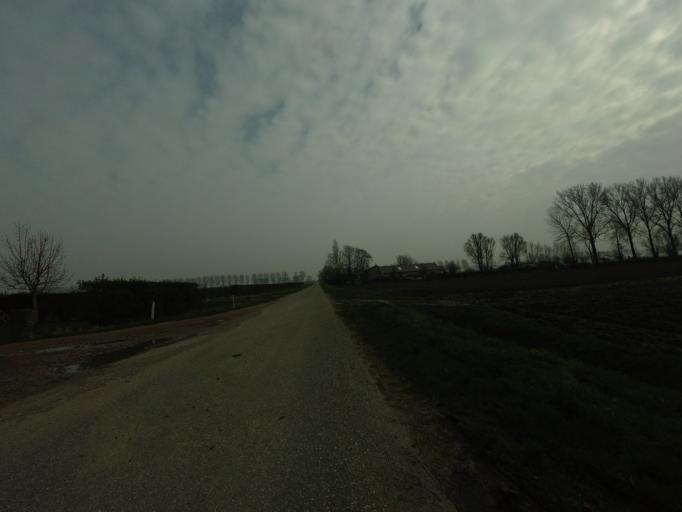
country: BE
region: Flanders
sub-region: Provincie Oost-Vlaanderen
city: Sint-Gillis-Waas
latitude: 51.3235
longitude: 4.1879
